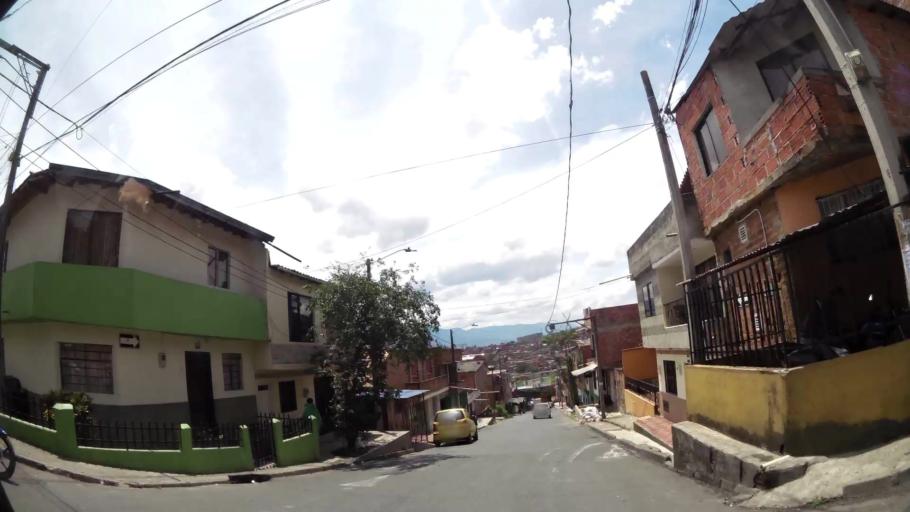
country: CO
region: Antioquia
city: Bello
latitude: 6.3489
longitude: -75.5627
